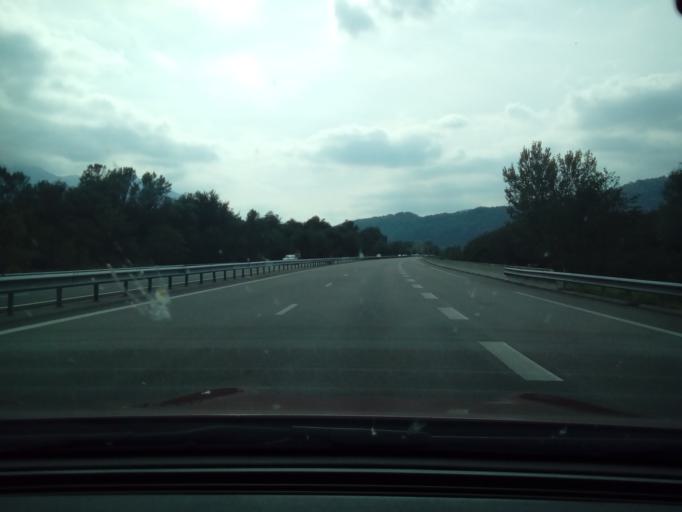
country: FR
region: Rhone-Alpes
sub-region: Departement de l'Isere
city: Tullins
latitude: 45.2407
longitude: 5.4970
